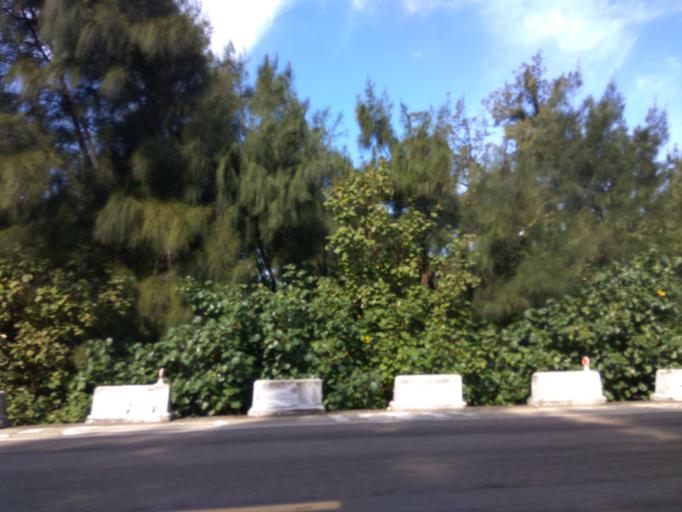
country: TW
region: Taiwan
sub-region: Hsinchu
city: Zhubei
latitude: 25.0299
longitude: 121.0473
